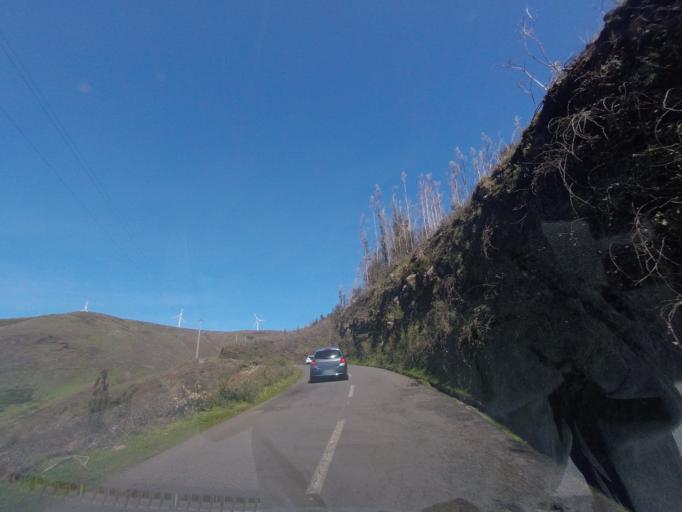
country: PT
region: Madeira
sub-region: Calheta
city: Arco da Calheta
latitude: 32.7367
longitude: -17.1037
